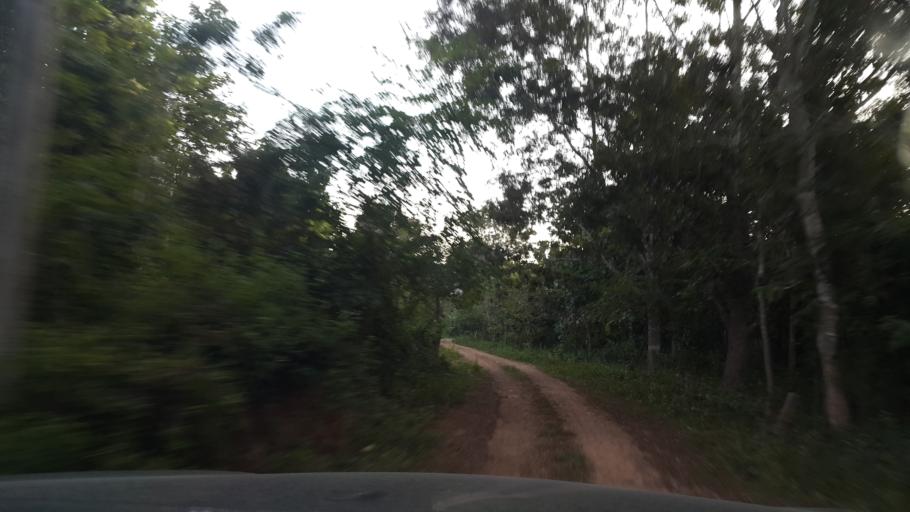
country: TH
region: Chiang Mai
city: Mae On
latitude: 18.6938
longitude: 99.2023
